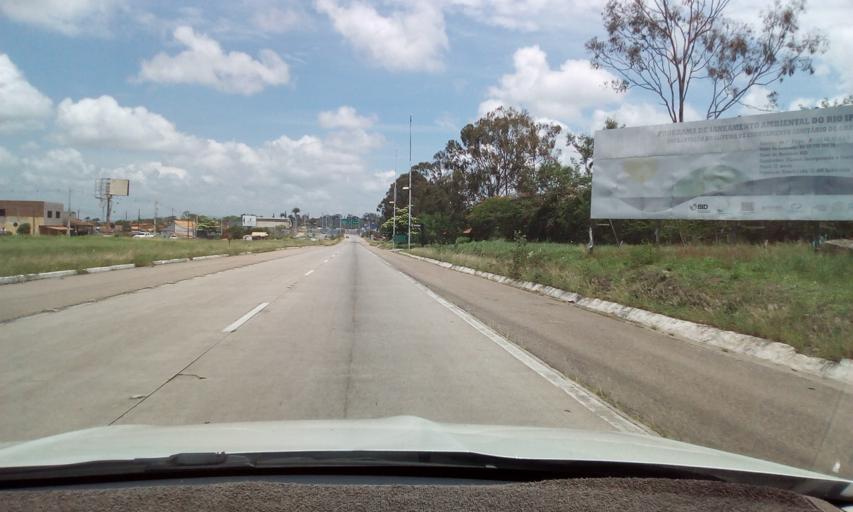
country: BR
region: Pernambuco
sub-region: Gravata
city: Gravata
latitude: -8.1945
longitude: -35.5385
